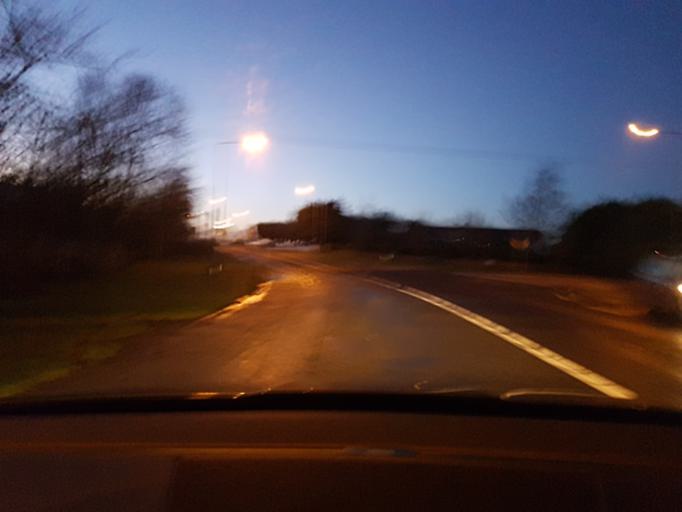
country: IE
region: Connaught
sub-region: Maigh Eo
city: Ballinrobe
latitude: 53.5826
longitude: -9.1240
